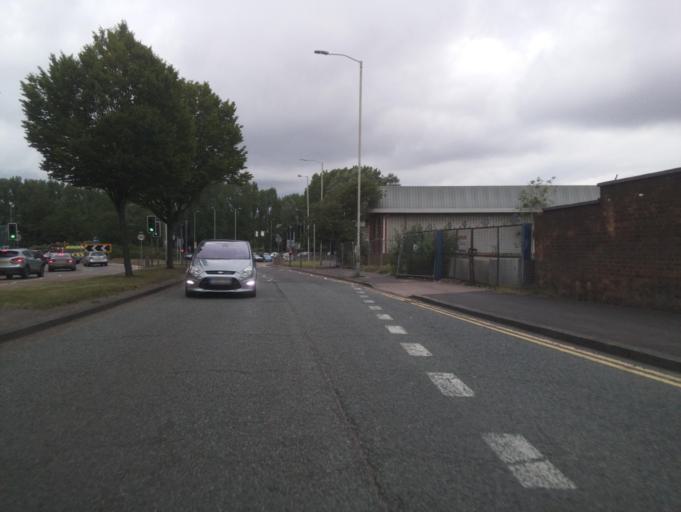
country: GB
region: England
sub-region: Wolverhampton
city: Wolverhampton
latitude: 52.5959
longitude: -2.1281
